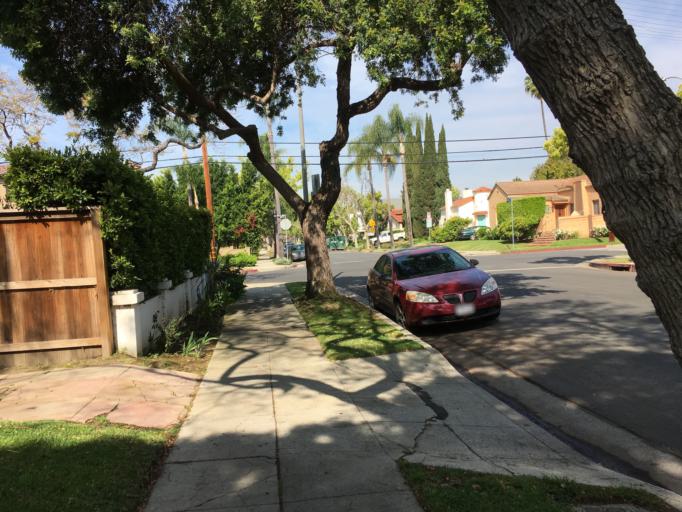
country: US
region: California
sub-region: Los Angeles County
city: West Hollywood
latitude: 34.0696
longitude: -118.3670
